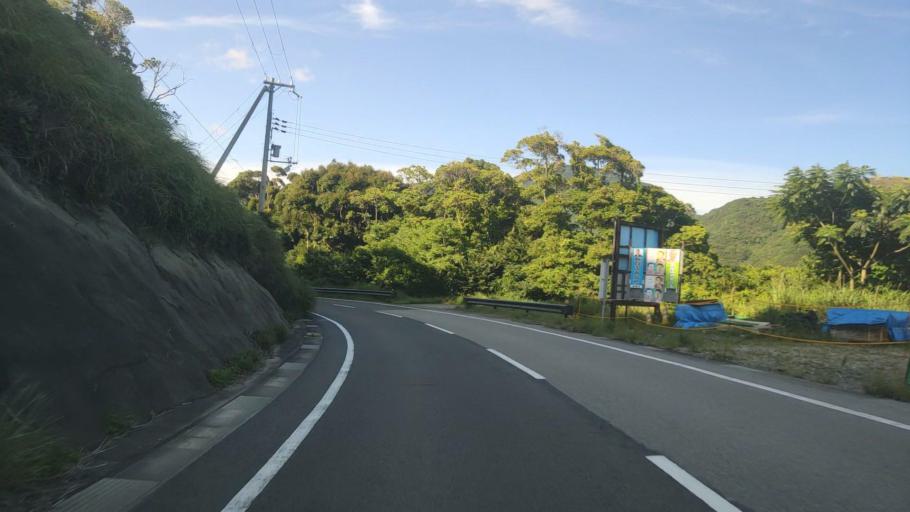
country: JP
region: Wakayama
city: Tanabe
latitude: 33.5100
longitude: 135.6021
